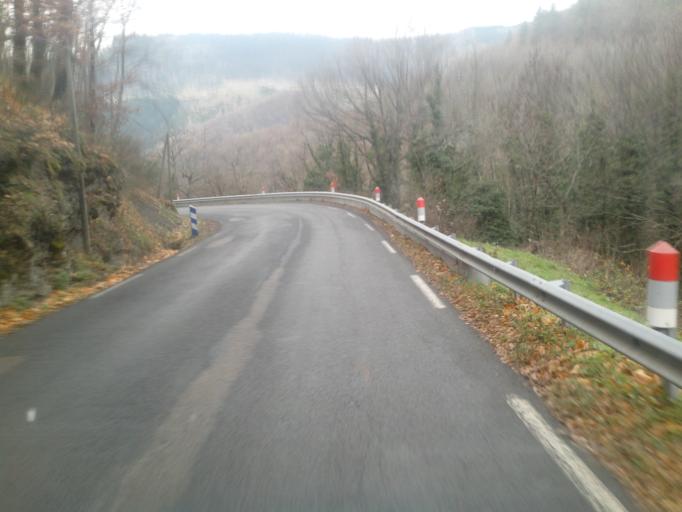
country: FR
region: Languedoc-Roussillon
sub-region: Departement de la Lozere
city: Florac
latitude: 44.3888
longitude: 3.5678
